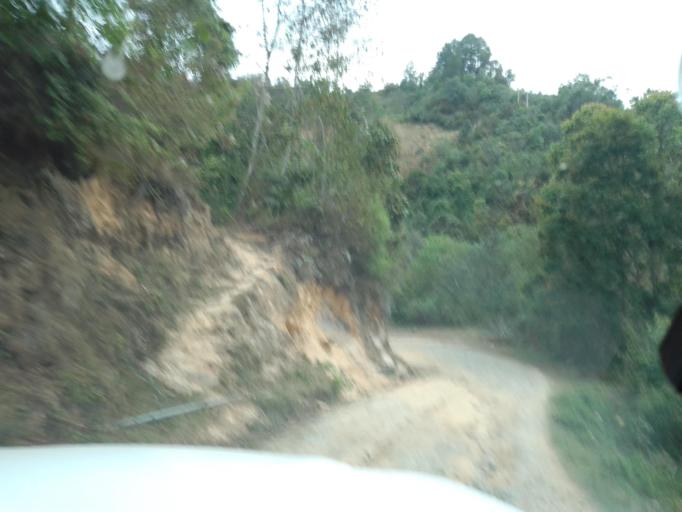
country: MX
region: Chiapas
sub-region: Cacahoatan
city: Benito Juarez
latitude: 15.2087
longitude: -92.2252
